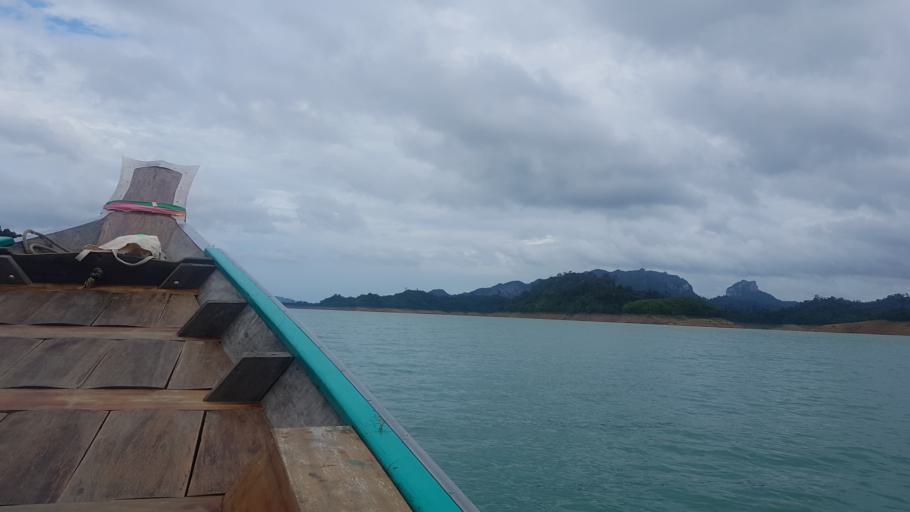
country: TH
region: Surat Thani
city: Ban Takhun
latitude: 8.9917
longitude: 98.7814
